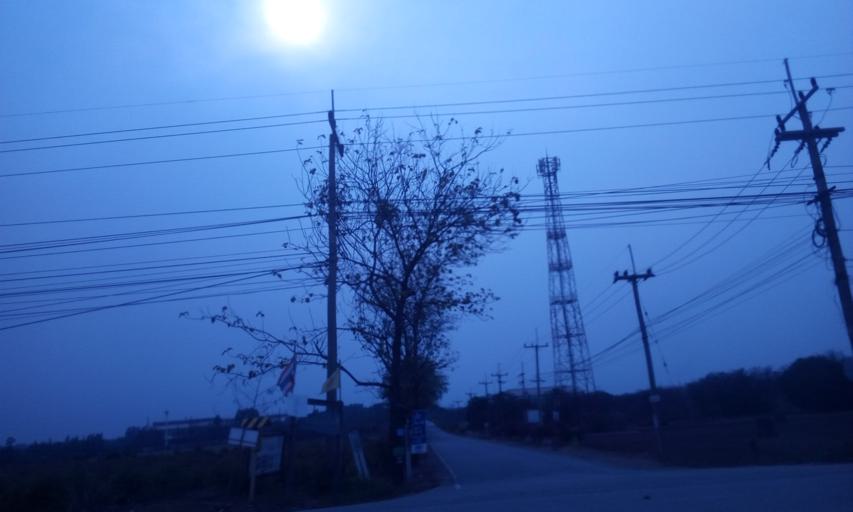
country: TH
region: Chachoengsao
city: Plaeng Yao
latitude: 13.5396
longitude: 101.2630
